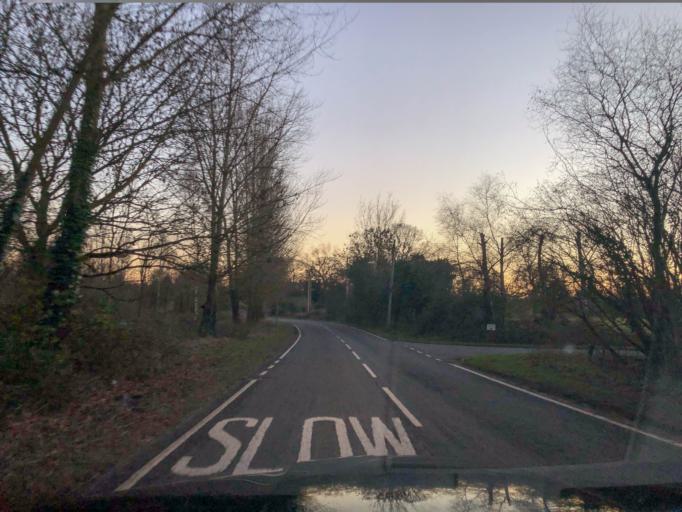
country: GB
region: England
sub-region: Warwickshire
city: Kenilworth
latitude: 52.3290
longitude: -1.5848
